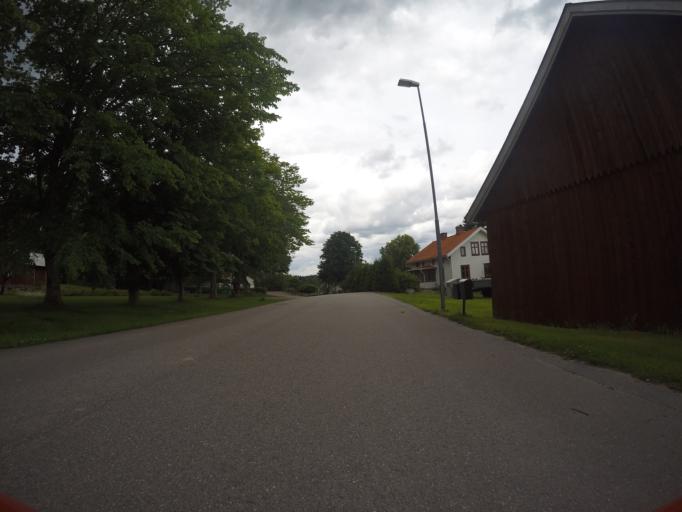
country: SE
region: Vaestra Goetaland
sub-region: Vanersborgs Kommun
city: Vargon
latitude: 58.2451
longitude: 12.4194
